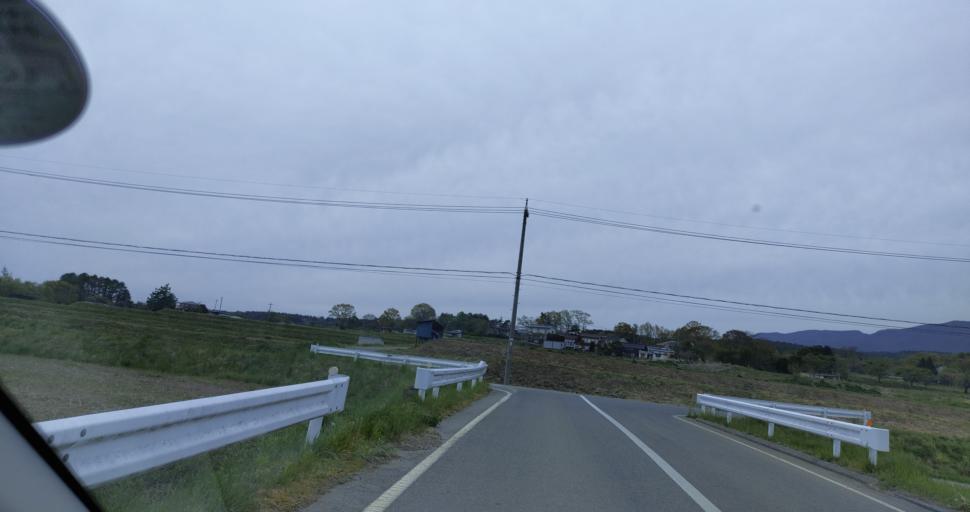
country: JP
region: Nagano
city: Komoro
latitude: 36.3341
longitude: 138.4869
